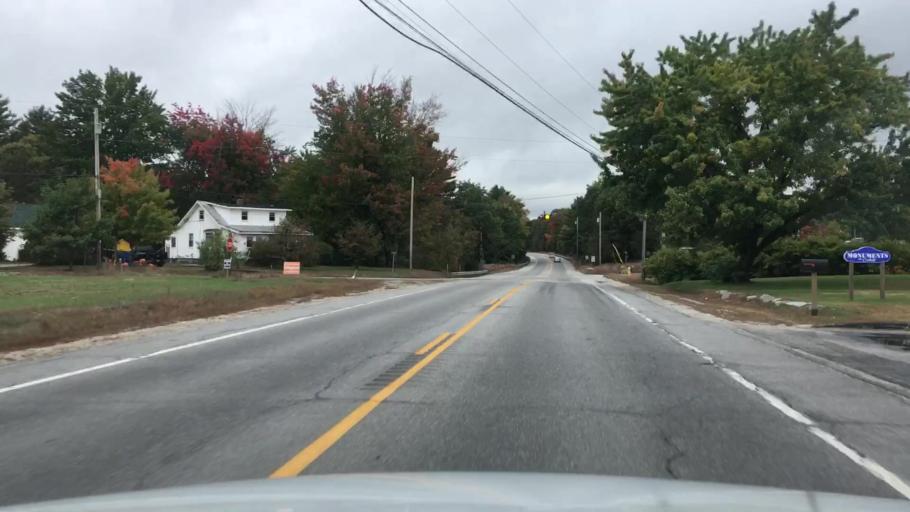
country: US
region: Maine
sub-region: Oxford County
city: Oxford
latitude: 44.1631
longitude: -70.4984
